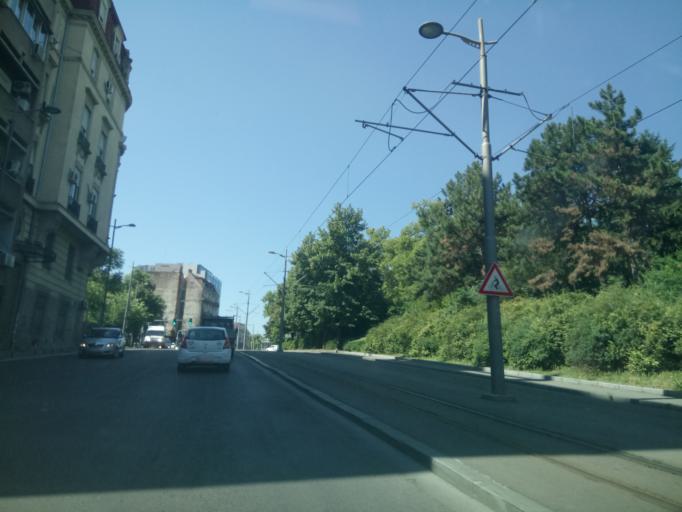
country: RS
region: Central Serbia
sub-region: Belgrade
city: Stari Grad
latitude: 44.8220
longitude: 20.4552
